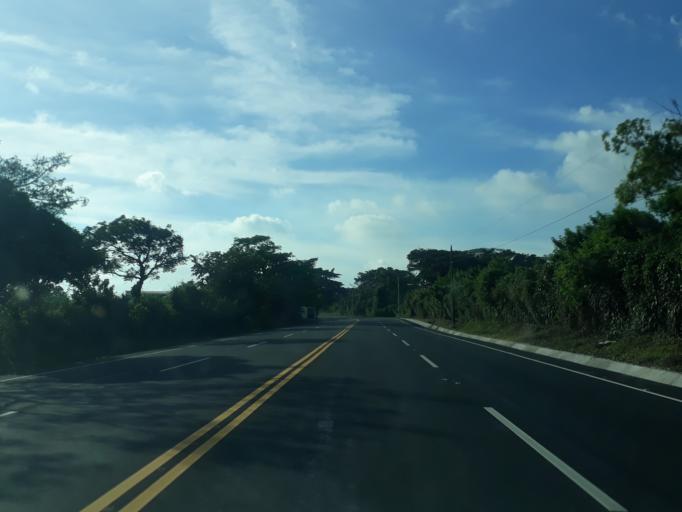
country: NI
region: Carazo
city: Diriamba
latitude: 11.9137
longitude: -86.2694
